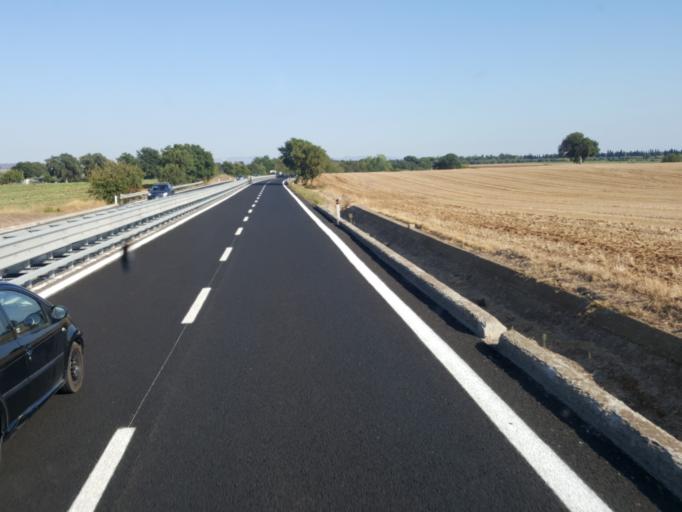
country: IT
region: Latium
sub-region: Provincia di Viterbo
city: Montalto di Castro
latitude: 42.2995
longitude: 11.6720
